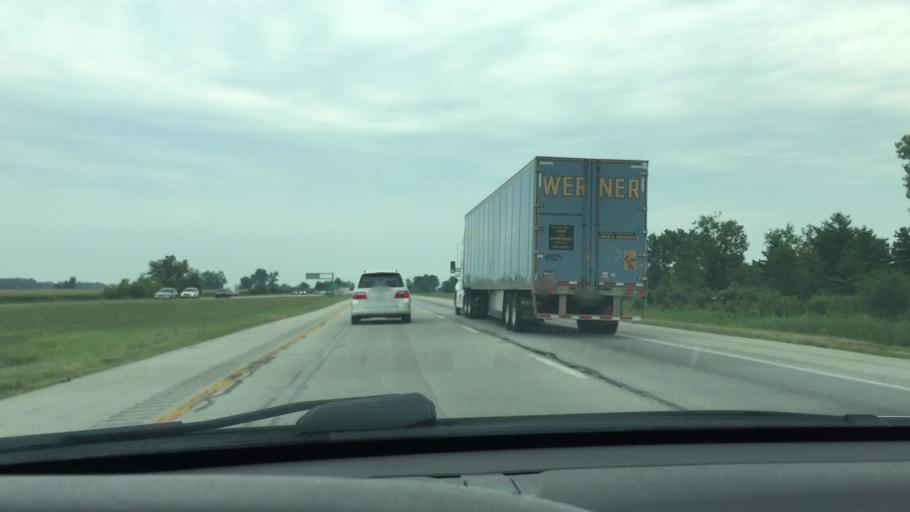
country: US
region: Ohio
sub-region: Greene County
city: Jamestown
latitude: 39.5870
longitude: -83.6689
